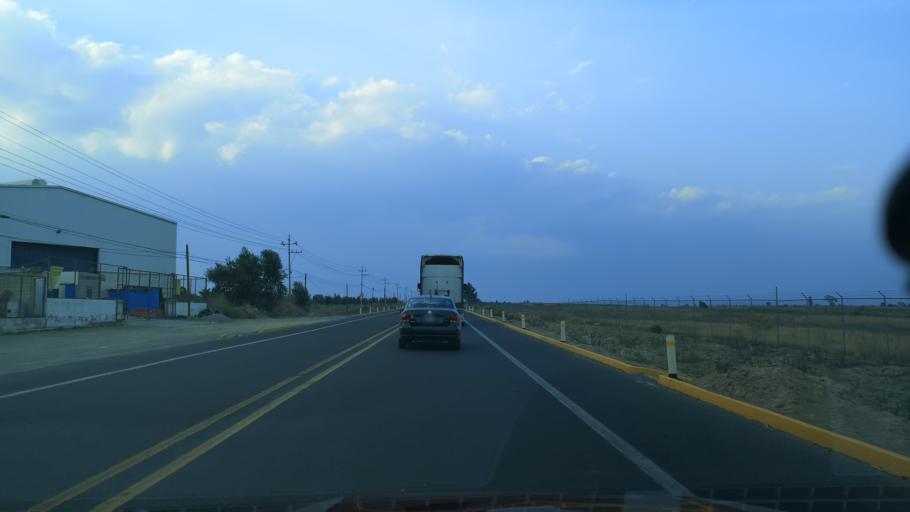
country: MX
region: Puebla
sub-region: Juan C. Bonilla
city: Santa Maria Zacatepec
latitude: 19.1436
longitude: -98.3740
